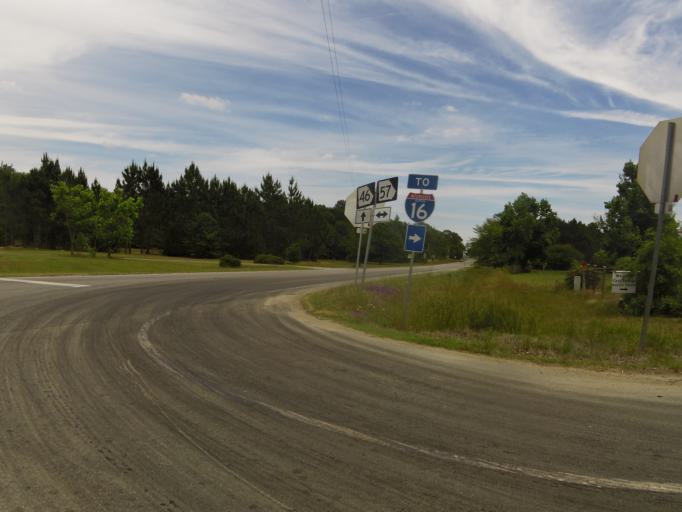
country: US
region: Georgia
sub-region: Candler County
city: Metter
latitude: 32.3771
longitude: -82.1666
